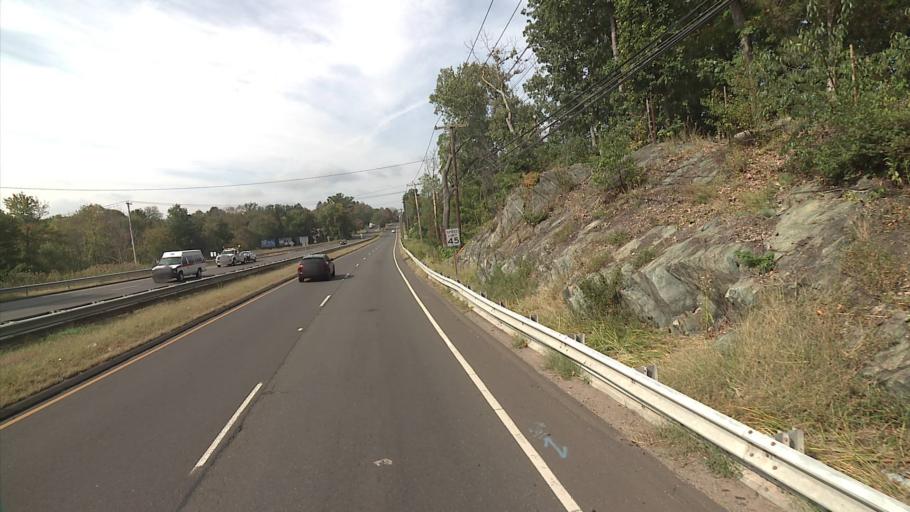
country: US
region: Connecticut
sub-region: New Haven County
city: Orange
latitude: 41.2992
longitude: -72.9963
